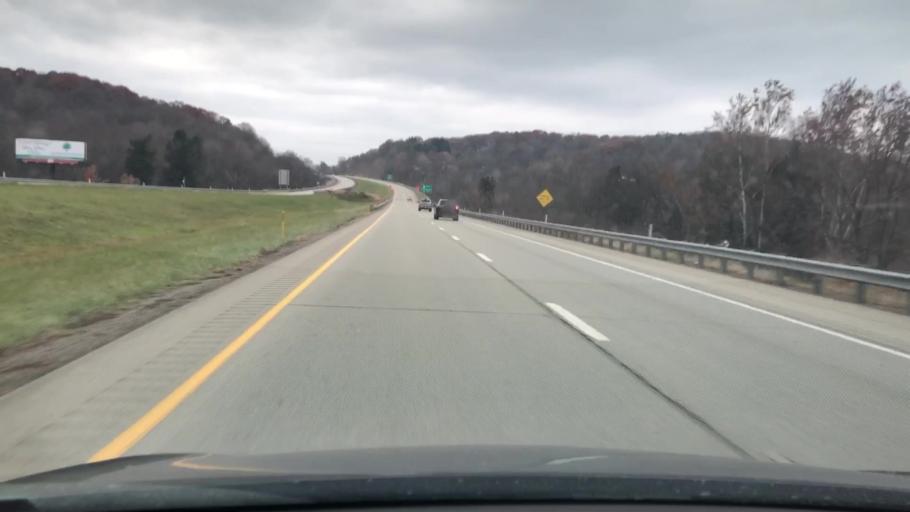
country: US
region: Pennsylvania
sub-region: Armstrong County
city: West Kittanning
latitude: 40.8033
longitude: -79.5331
